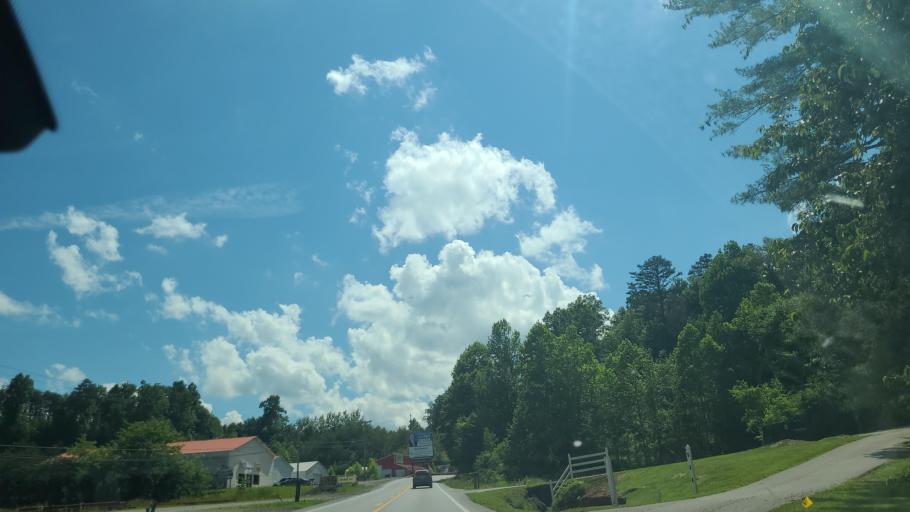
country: US
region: Kentucky
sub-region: Whitley County
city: Corbin
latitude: 36.9135
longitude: -84.1400
